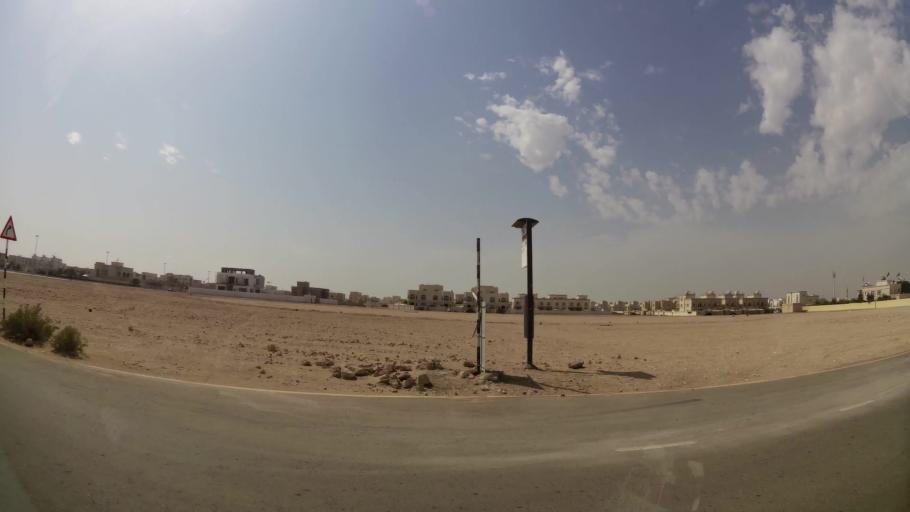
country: AE
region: Abu Dhabi
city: Abu Dhabi
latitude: 24.3348
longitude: 54.5679
